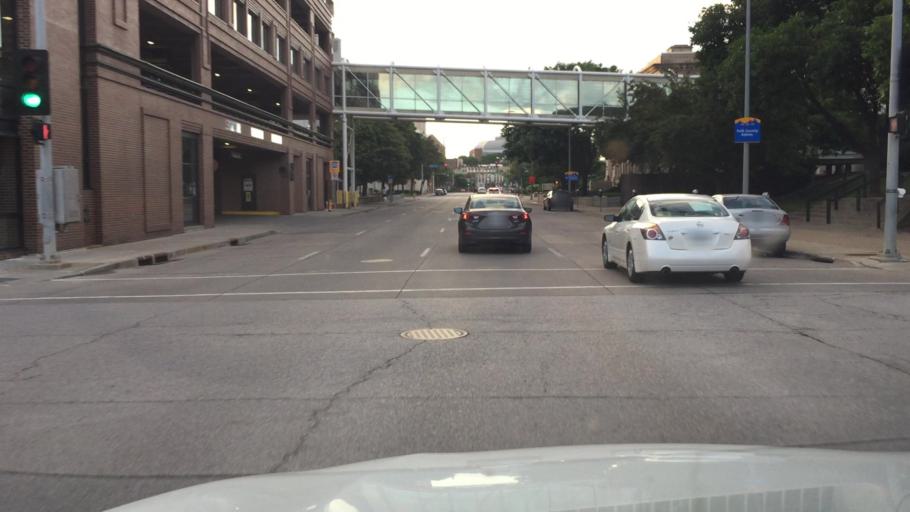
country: US
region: Iowa
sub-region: Polk County
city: Des Moines
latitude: 41.5856
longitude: -93.6193
